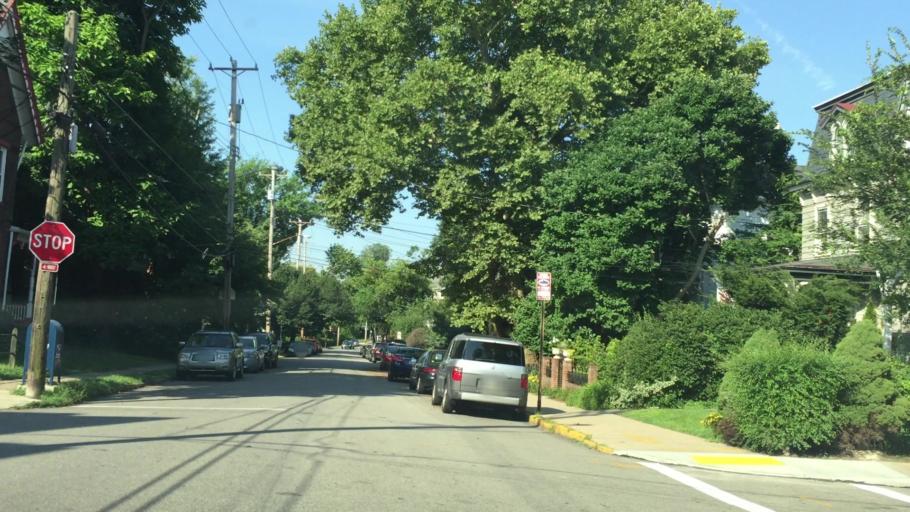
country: US
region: Pennsylvania
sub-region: Allegheny County
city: Bloomfield
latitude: 40.4551
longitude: -79.9238
